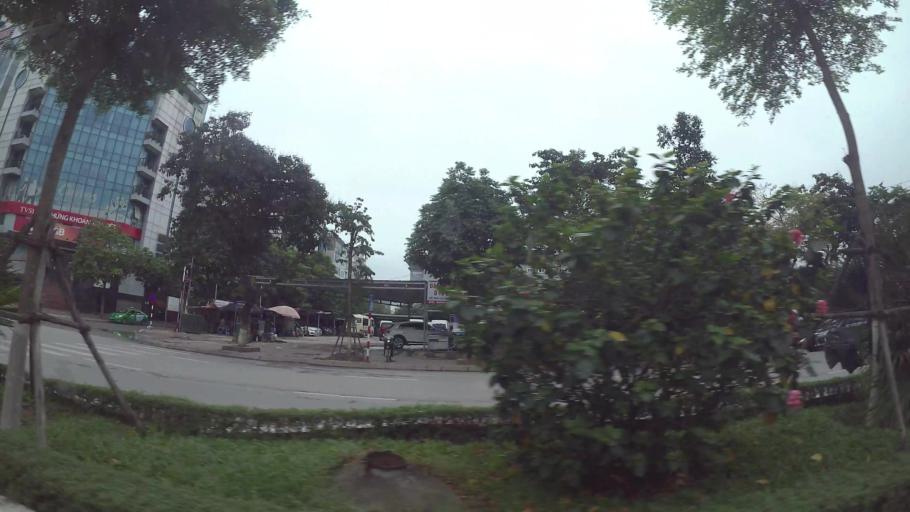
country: VN
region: Ha Noi
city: Cau Giay
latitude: 21.0314
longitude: 105.7886
